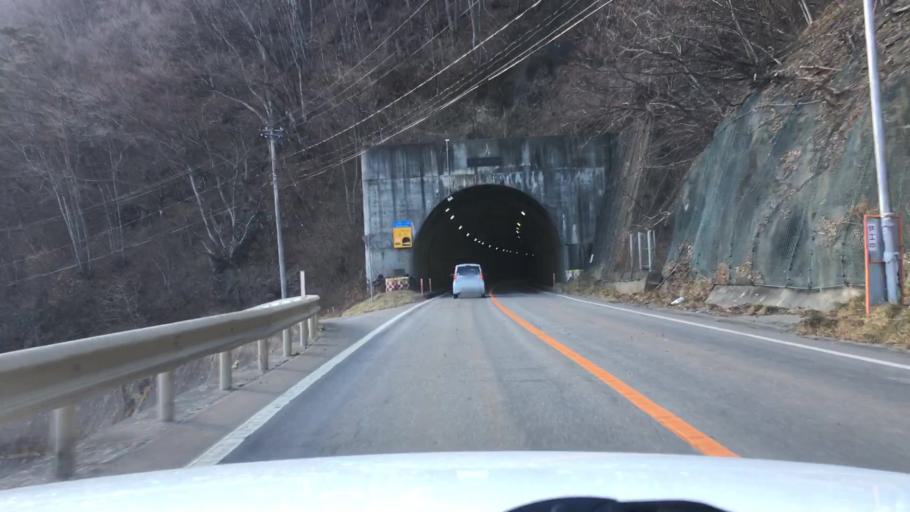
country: JP
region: Iwate
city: Miyako
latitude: 39.5977
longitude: 141.7528
